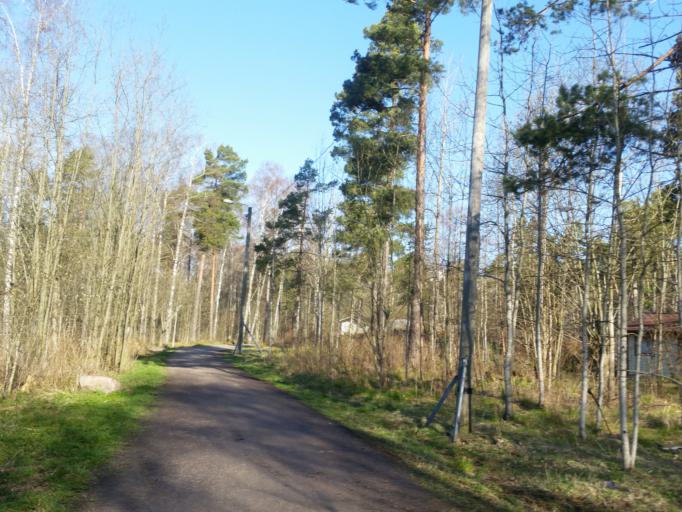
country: FI
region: Uusimaa
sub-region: Helsinki
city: Helsinki
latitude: 60.1460
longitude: 24.8855
